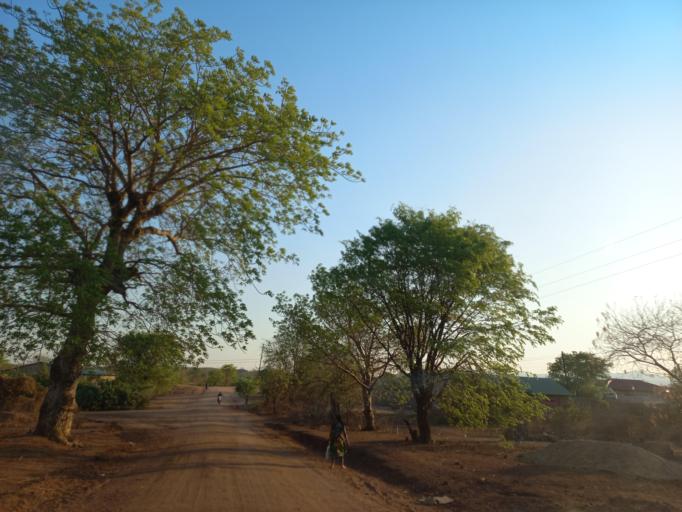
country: ZM
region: Lusaka
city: Luangwa
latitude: -15.6183
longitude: 30.3903
